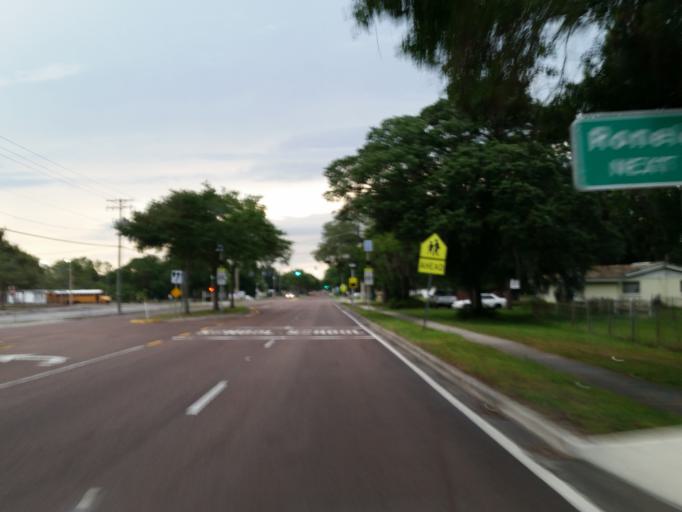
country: US
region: Florida
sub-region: Hillsborough County
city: Brandon
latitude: 27.8972
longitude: -82.2939
